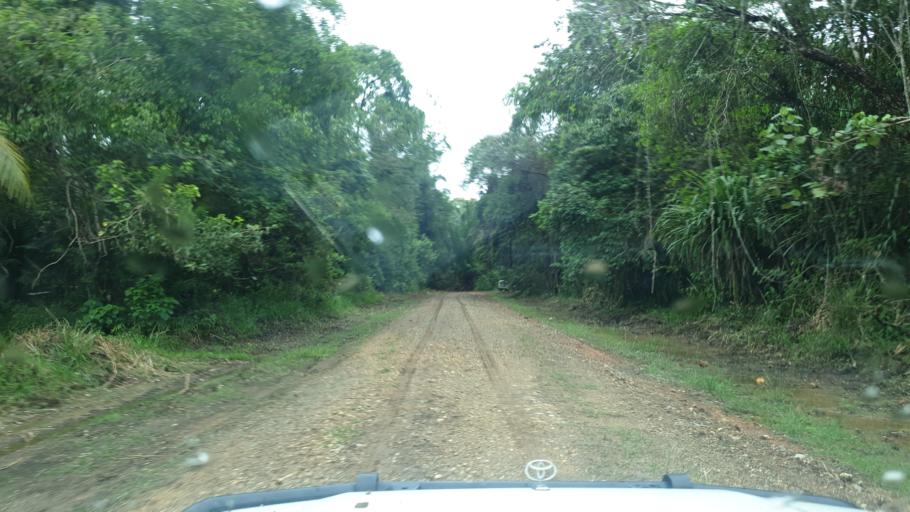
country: PG
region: Gulf
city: Kerema
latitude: -7.9559
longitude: 145.8394
